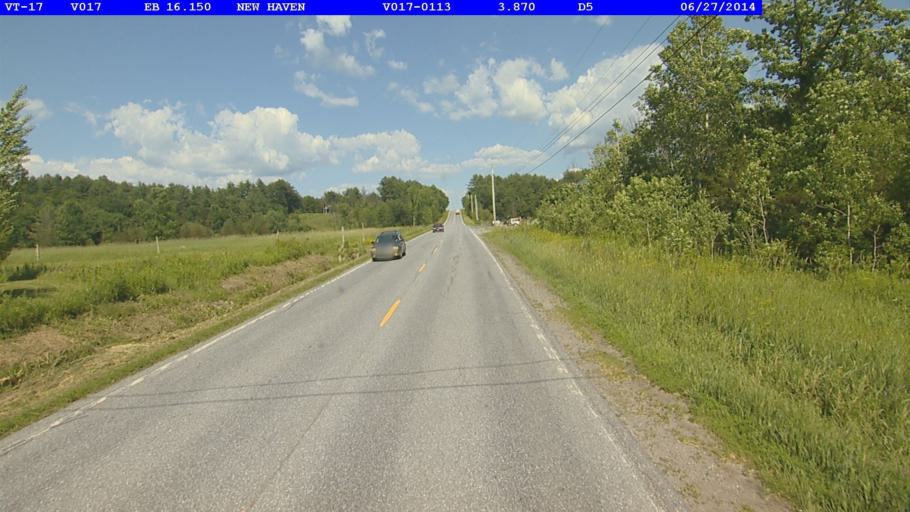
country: US
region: Vermont
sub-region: Addison County
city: Vergennes
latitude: 44.1225
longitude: -73.1734
